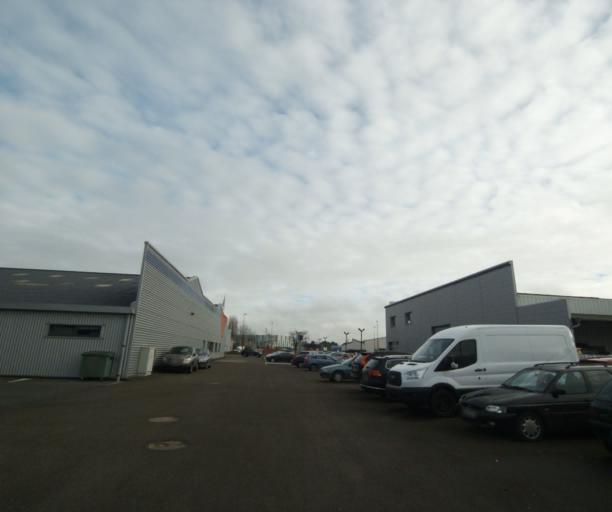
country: FR
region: Pays de la Loire
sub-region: Departement de la Sarthe
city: Allonnes
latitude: 47.9745
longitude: 0.1721
